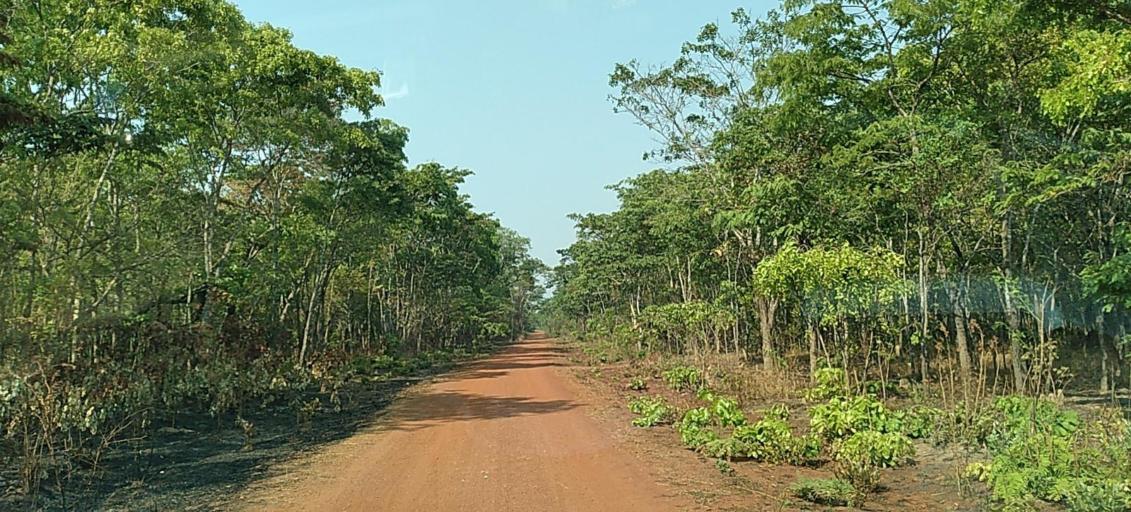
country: ZM
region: Copperbelt
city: Chingola
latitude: -12.8699
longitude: 27.4542
